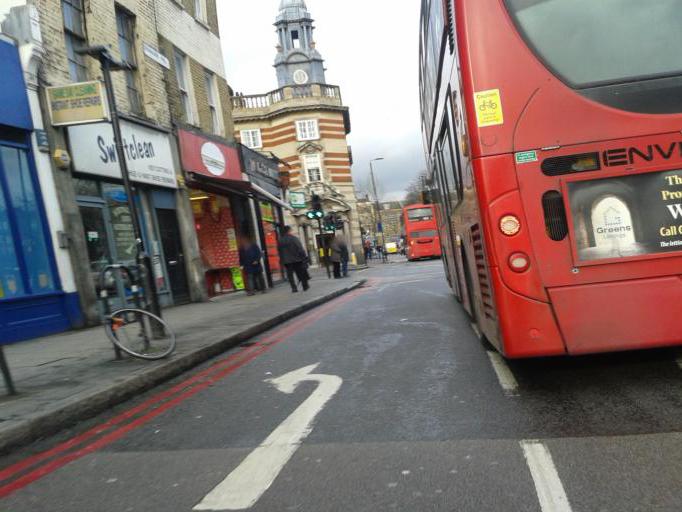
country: GB
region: England
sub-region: Greater London
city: Camberwell
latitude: 51.4736
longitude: -0.0931
